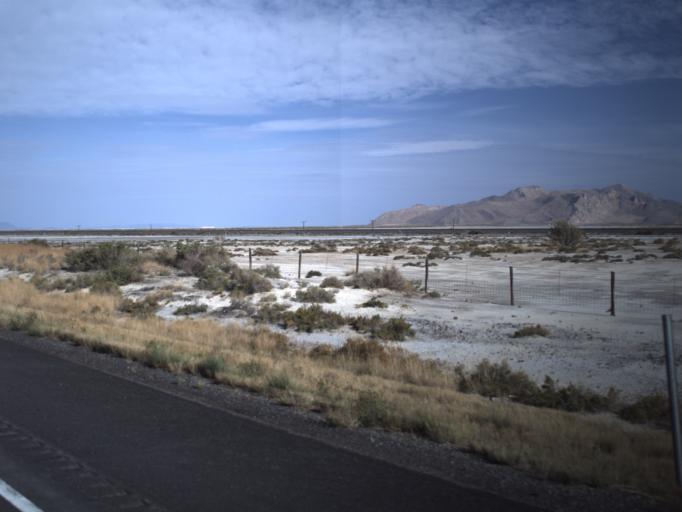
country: US
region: Utah
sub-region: Tooele County
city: Grantsville
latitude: 40.6929
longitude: -112.4668
